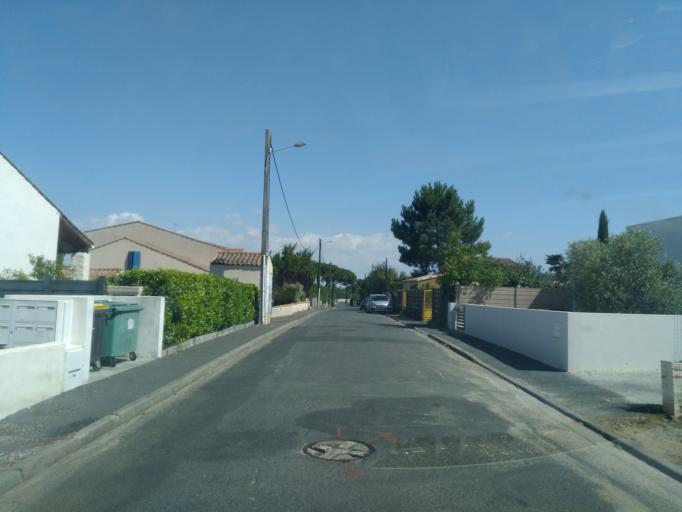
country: FR
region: Poitou-Charentes
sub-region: Departement de la Charente-Maritime
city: Saint-Palais-sur-Mer
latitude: 45.6464
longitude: -1.0829
